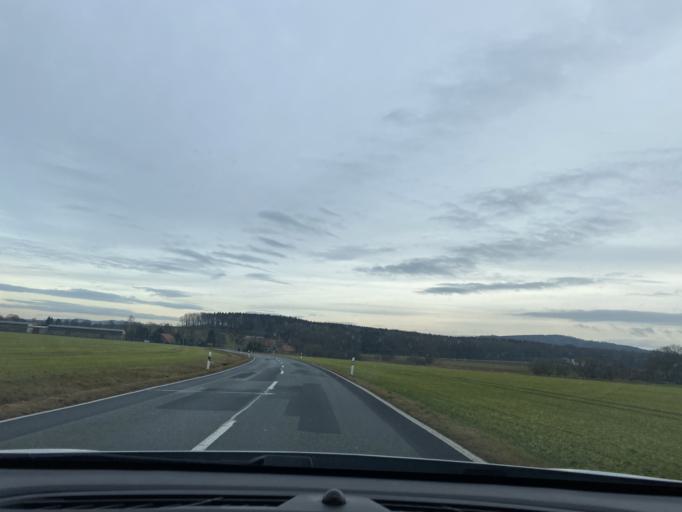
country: DE
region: Saxony
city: Reichenbach
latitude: 51.1188
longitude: 14.8301
